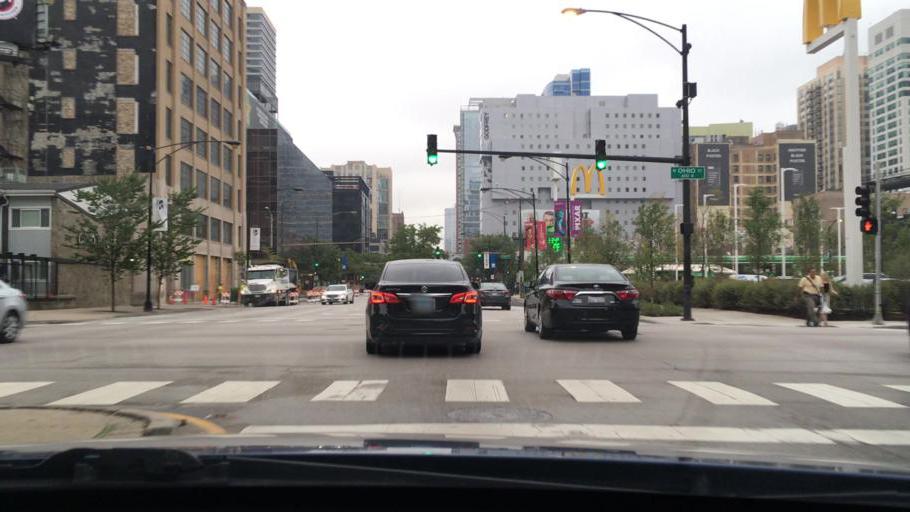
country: US
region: Illinois
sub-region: Cook County
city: Chicago
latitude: 41.8922
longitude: -87.6326
